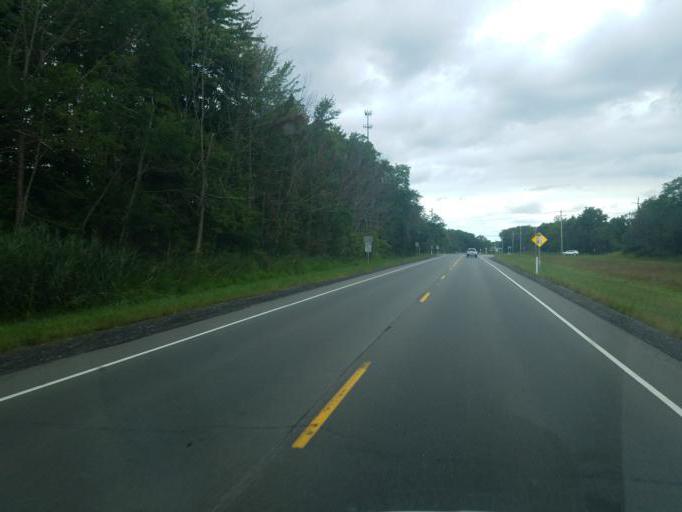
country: US
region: Ohio
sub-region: Lake County
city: Painesville
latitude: 41.6393
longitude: -81.2411
